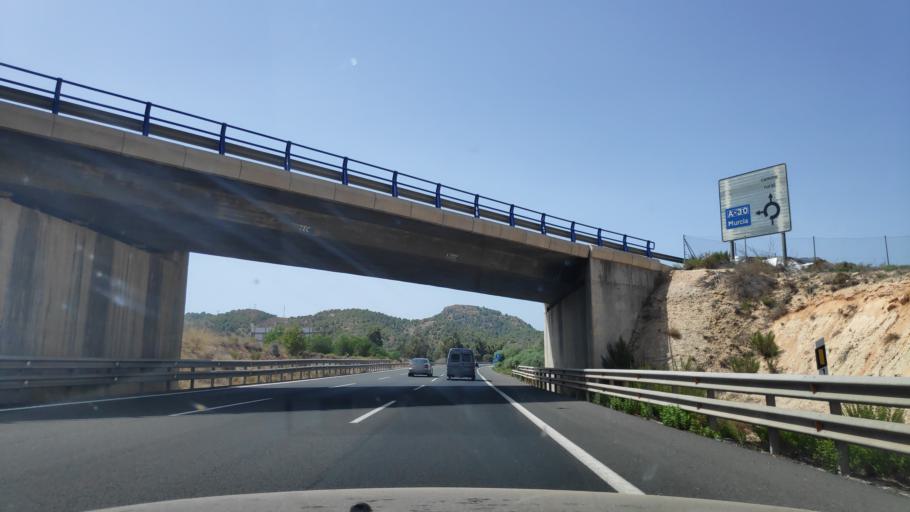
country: ES
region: Murcia
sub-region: Murcia
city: Murcia
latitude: 37.8857
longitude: -1.1382
